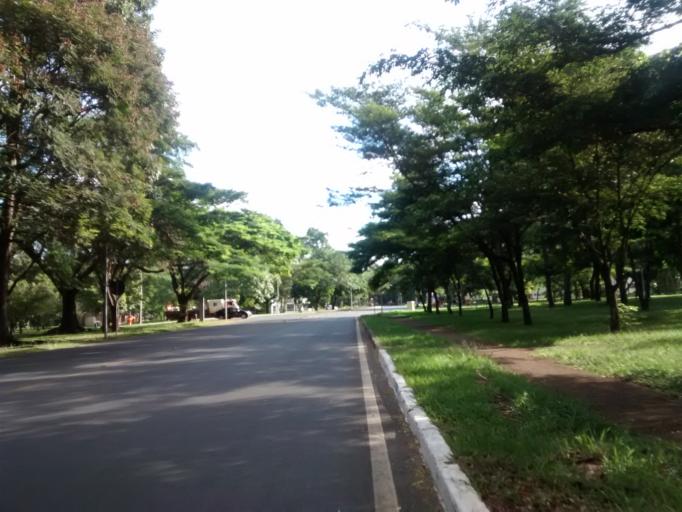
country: BR
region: Federal District
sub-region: Brasilia
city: Brasilia
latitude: -15.8094
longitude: -47.8972
